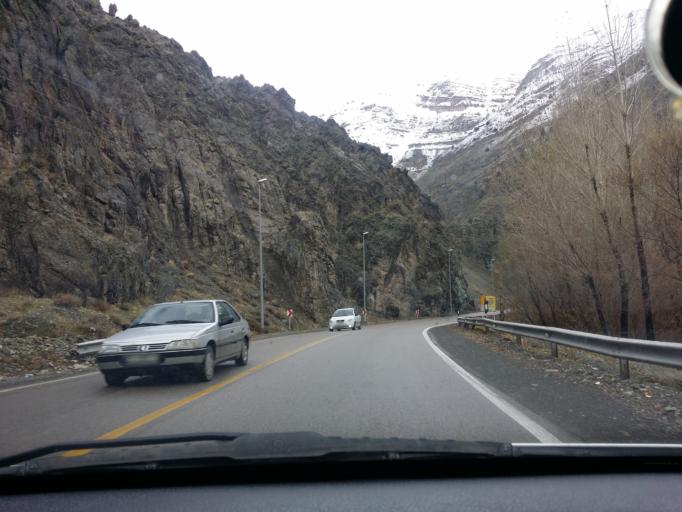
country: IR
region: Tehran
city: Tajrish
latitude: 36.0162
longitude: 51.2954
